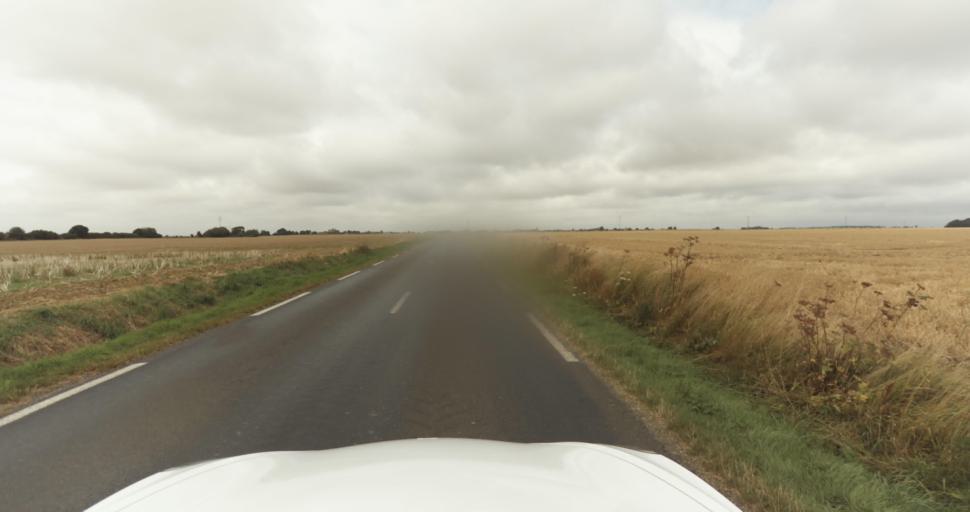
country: FR
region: Haute-Normandie
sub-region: Departement de l'Eure
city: Claville
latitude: 49.0781
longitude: 1.0591
